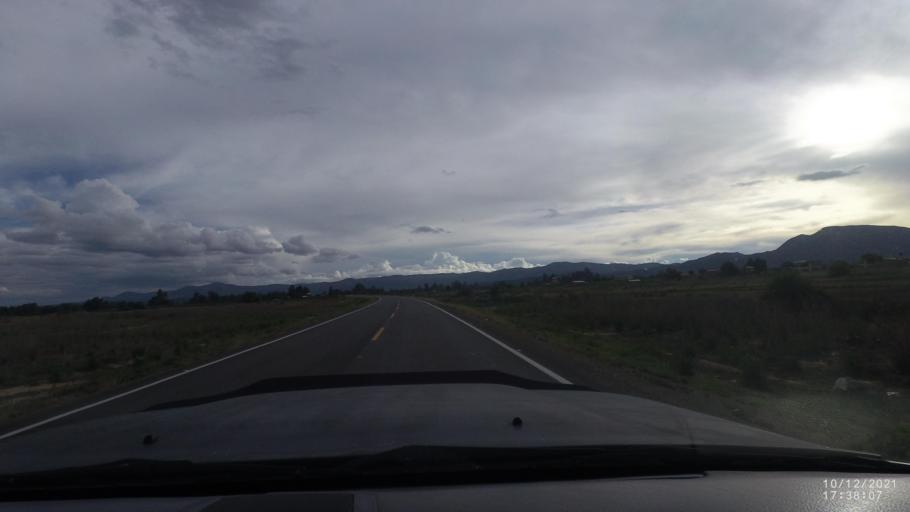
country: BO
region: Cochabamba
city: Tarata
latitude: -17.5659
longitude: -66.0087
